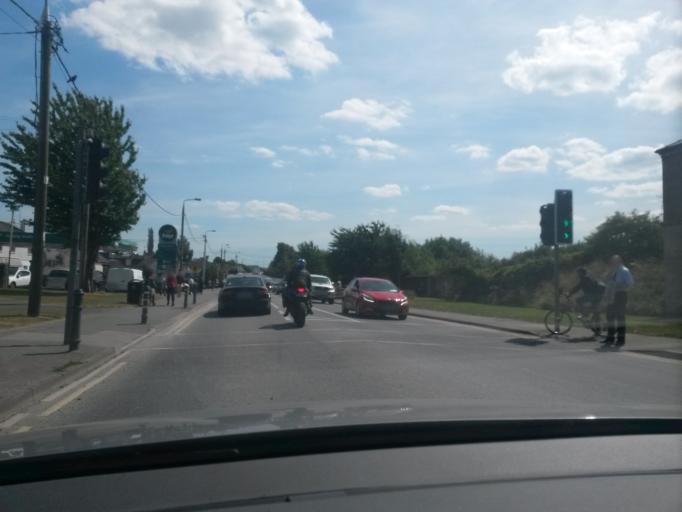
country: IE
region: Leinster
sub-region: Kildare
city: Sallins
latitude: 53.2509
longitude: -6.6652
